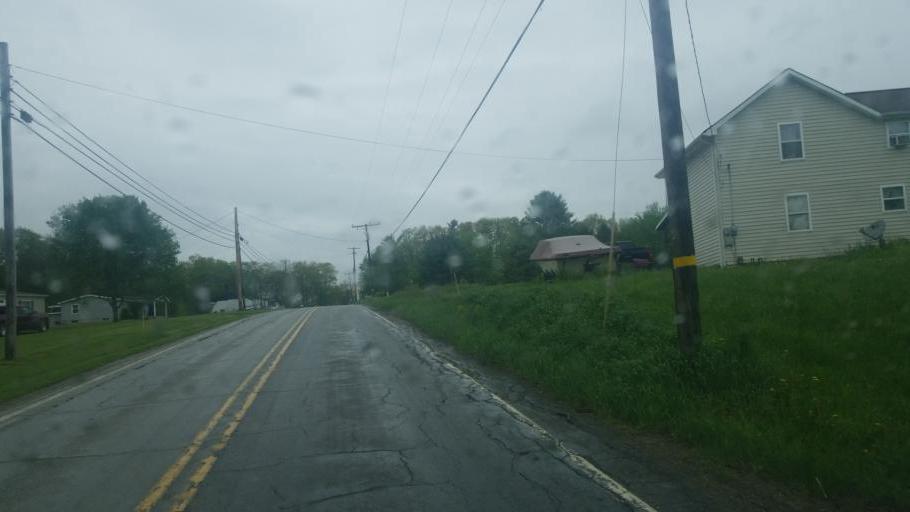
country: US
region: Pennsylvania
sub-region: Clarion County
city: Marianne
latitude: 41.3800
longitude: -79.3145
